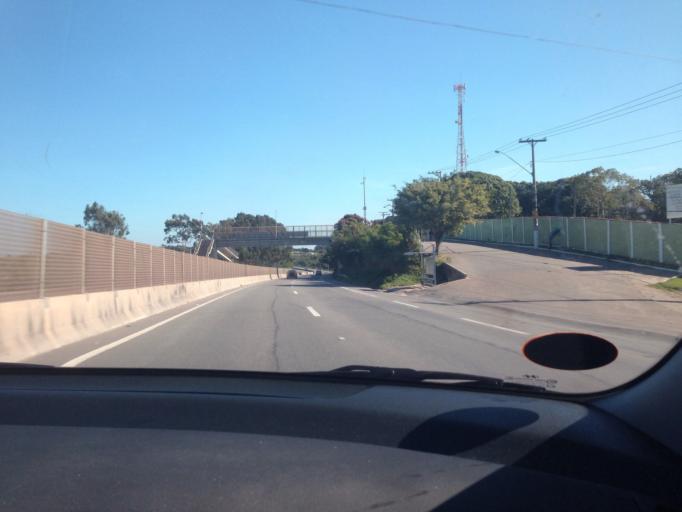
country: BR
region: Espirito Santo
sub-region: Viana
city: Viana
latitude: -20.4969
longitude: -40.3591
